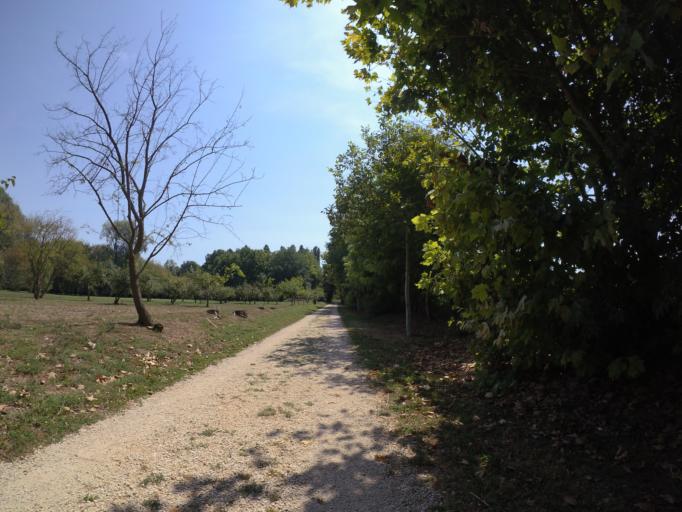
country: IT
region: Friuli Venezia Giulia
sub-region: Provincia di Udine
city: Codroipo
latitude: 45.9542
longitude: 12.9785
